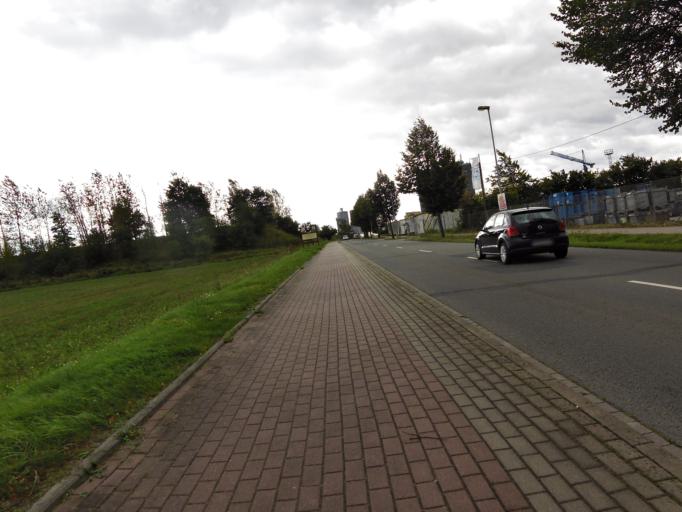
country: DE
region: Saxony-Anhalt
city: Tangermunde
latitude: 52.5629
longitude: 11.9803
